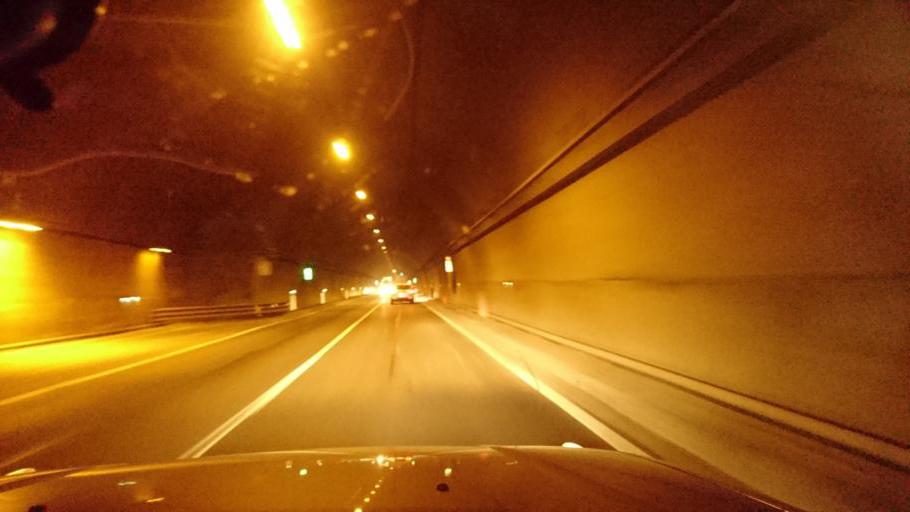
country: IT
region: Lombardy
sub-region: Provincia di Brescia
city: Roe Volciano
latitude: 45.6148
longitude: 10.4773
